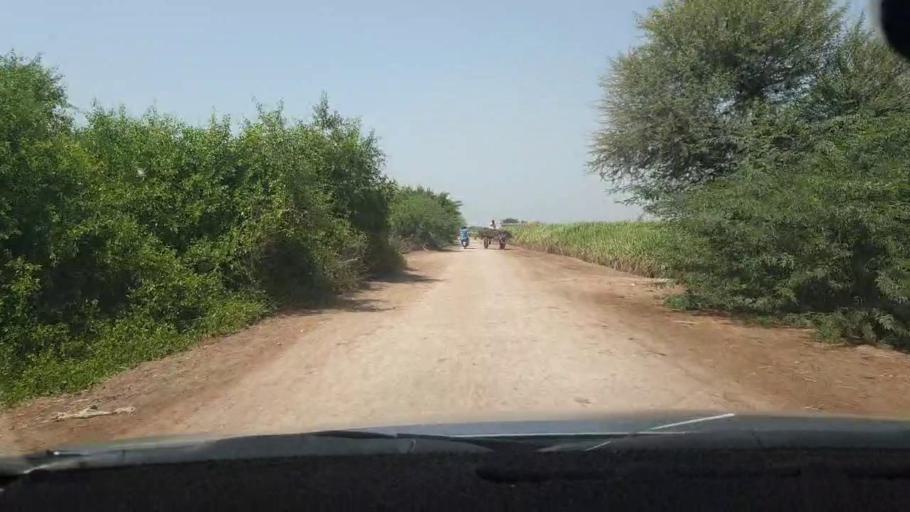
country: PK
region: Sindh
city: Tando Mittha Khan
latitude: 25.8535
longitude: 69.4206
